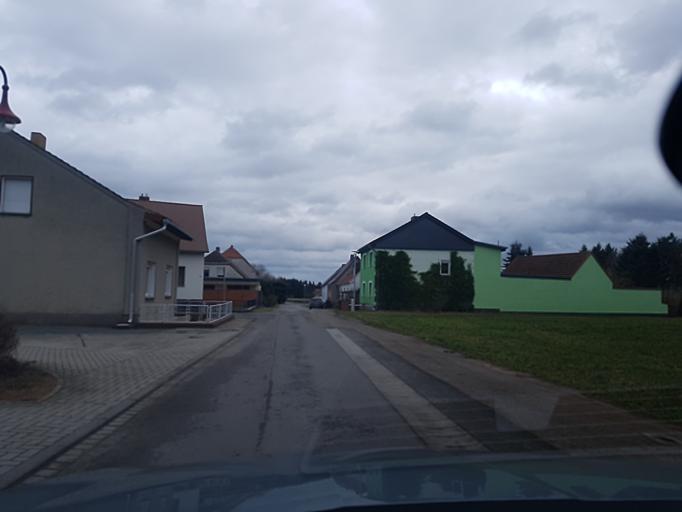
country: DE
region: Brandenburg
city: Schonborn
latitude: 51.5992
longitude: 13.4954
